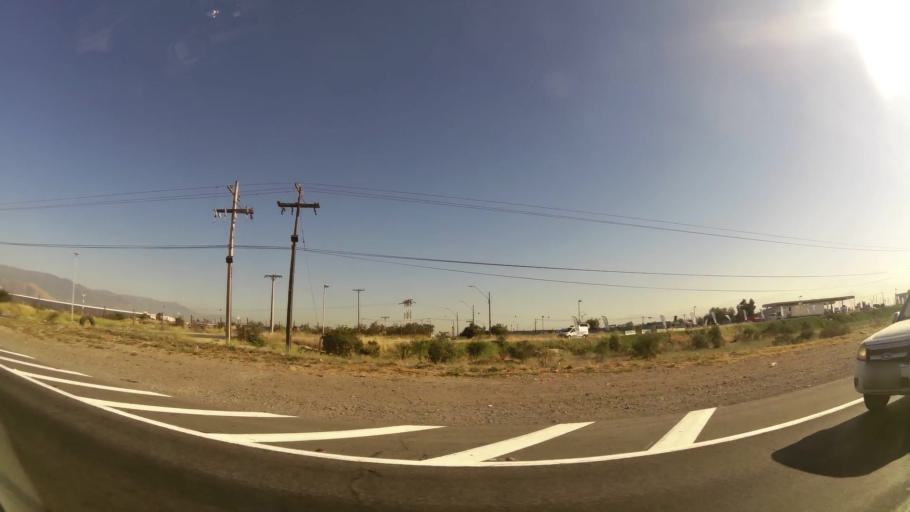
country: CL
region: Santiago Metropolitan
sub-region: Provincia de Santiago
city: Lo Prado
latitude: -33.4430
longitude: -70.7927
